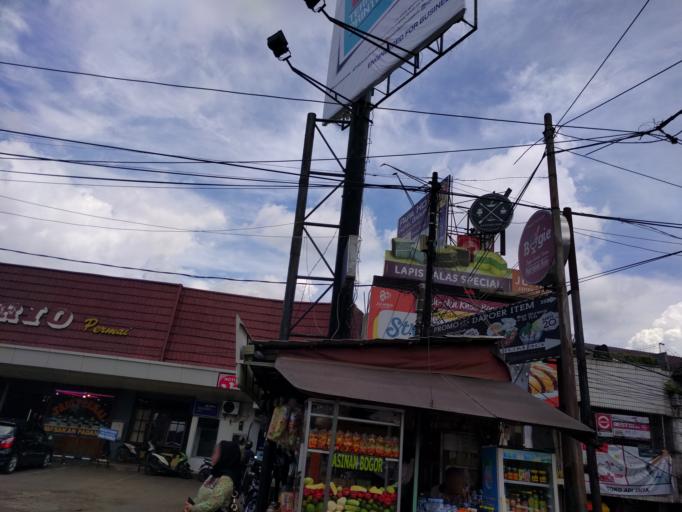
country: ID
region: West Java
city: Bogor
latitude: -6.6032
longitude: 106.8059
